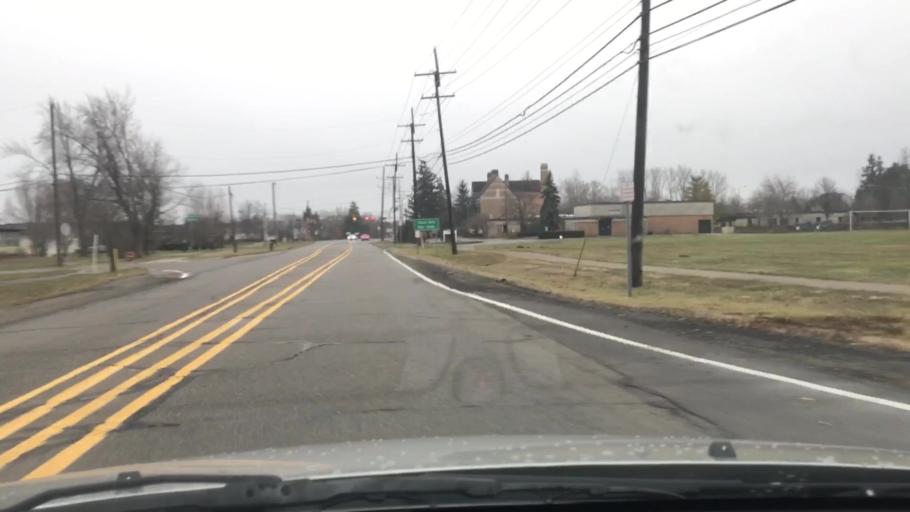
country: US
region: Michigan
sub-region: Oakland County
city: Troy
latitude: 42.6247
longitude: -83.1510
